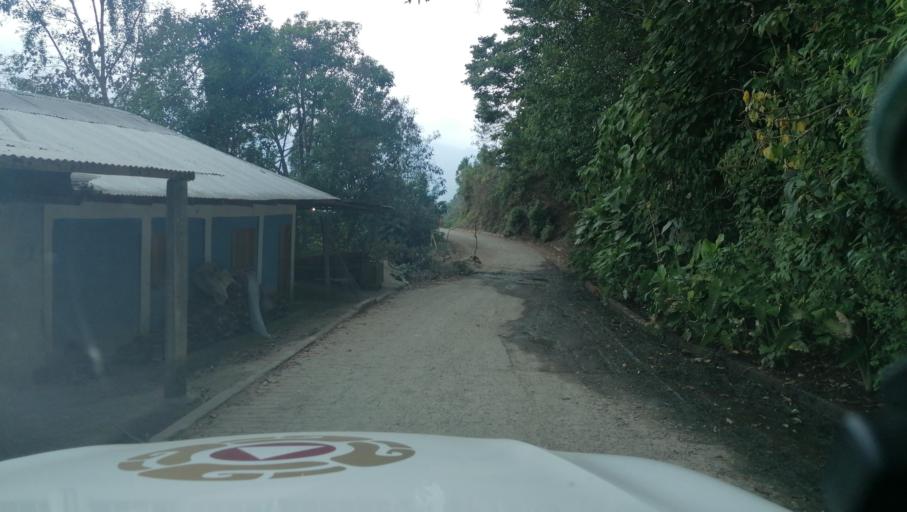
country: GT
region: San Marcos
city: Tacana
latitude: 15.1995
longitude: -92.1770
